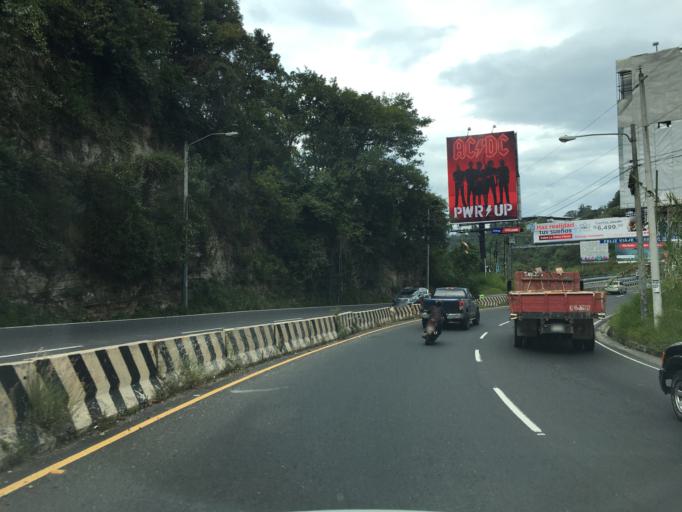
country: GT
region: Guatemala
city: Mixco
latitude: 14.5918
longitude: -90.5745
